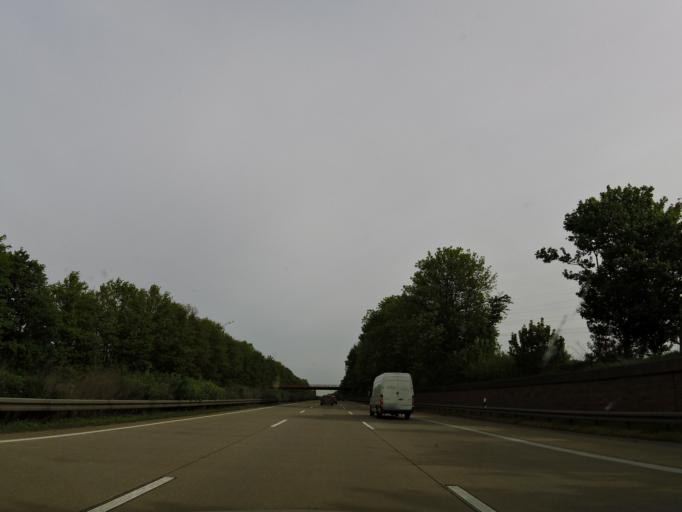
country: DE
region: Lower Saxony
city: Algermissen
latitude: 52.2624
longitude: 9.9167
